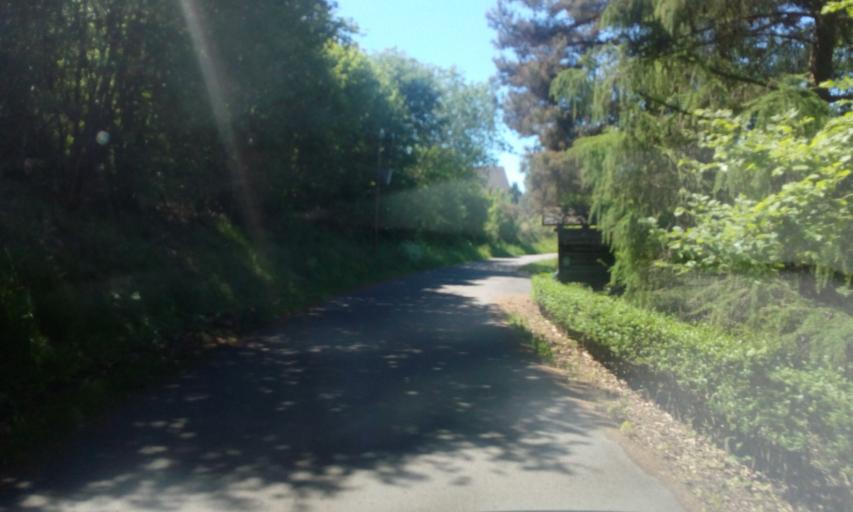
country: DE
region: Rheinland-Pfalz
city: Trittenheim
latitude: 49.8097
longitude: 6.8982
